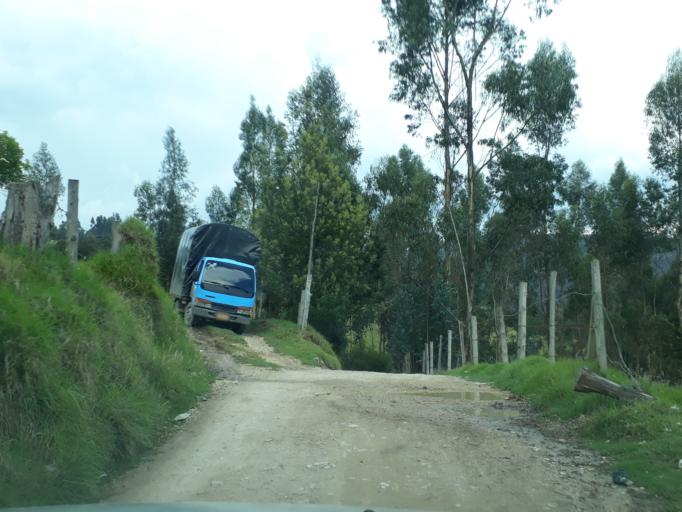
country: CO
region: Cundinamarca
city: Lenguazaque
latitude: 5.2632
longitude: -73.6965
